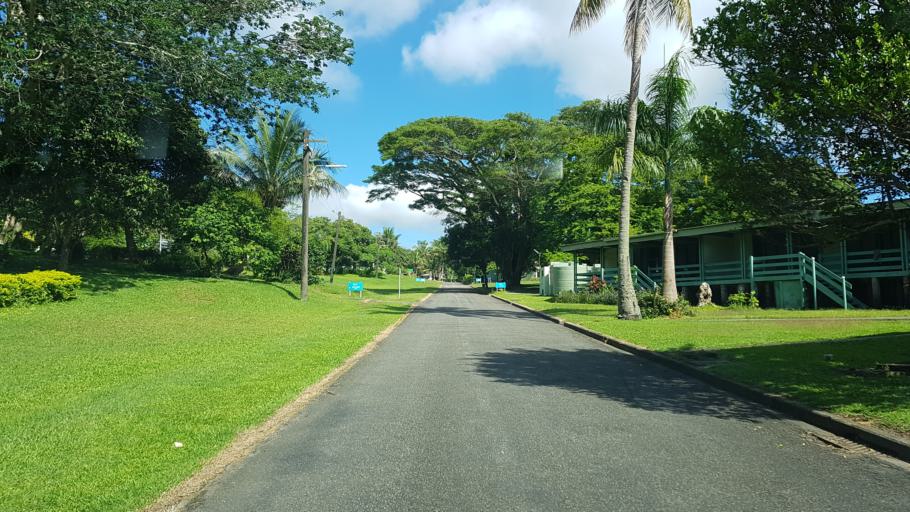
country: FJ
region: Central
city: Suva
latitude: -18.1530
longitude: 178.4427
